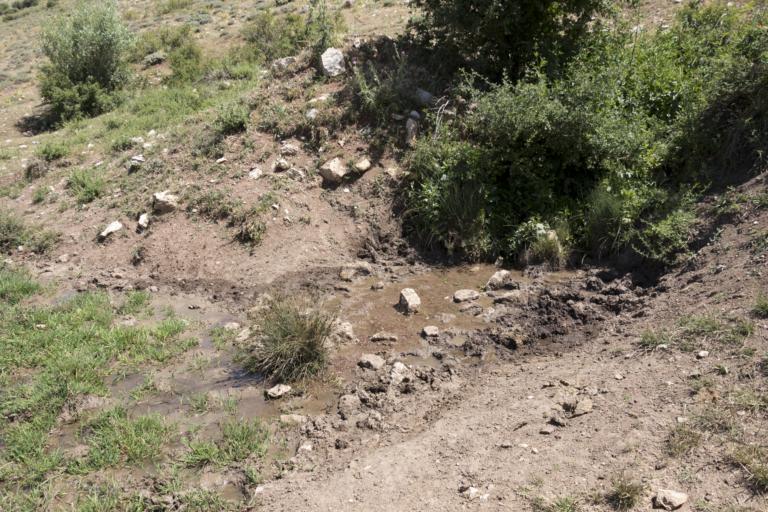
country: TR
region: Kayseri
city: Toklar
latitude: 38.4154
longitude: 36.1136
